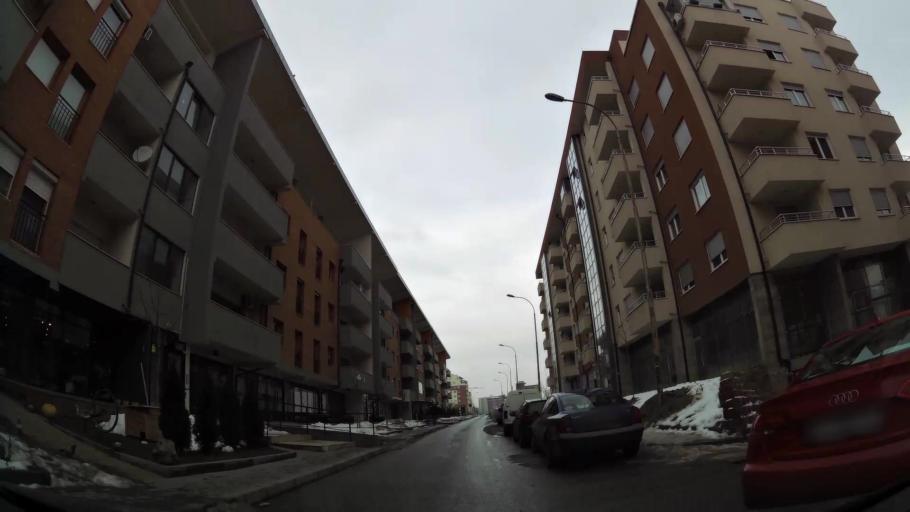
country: XK
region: Pristina
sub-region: Komuna e Prishtines
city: Pristina
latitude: 42.6575
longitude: 21.1482
